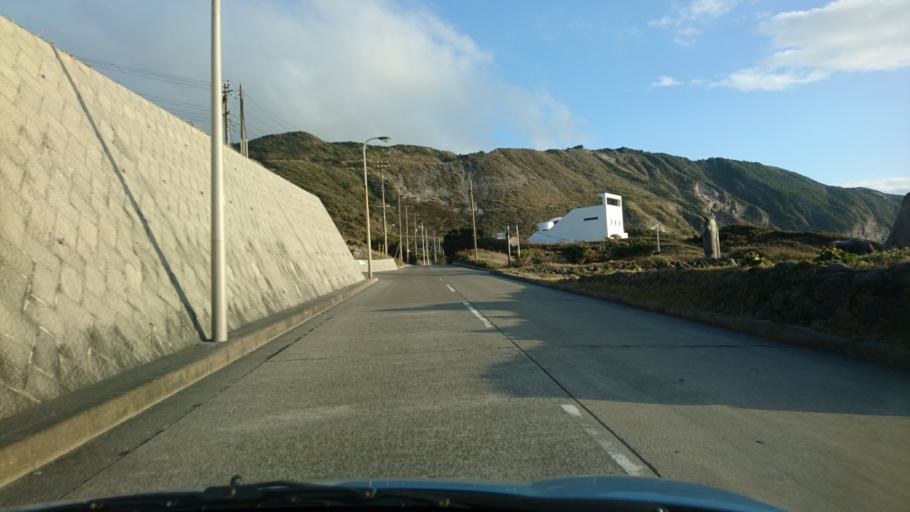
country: JP
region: Shizuoka
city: Shimoda
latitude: 34.3618
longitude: 139.2448
